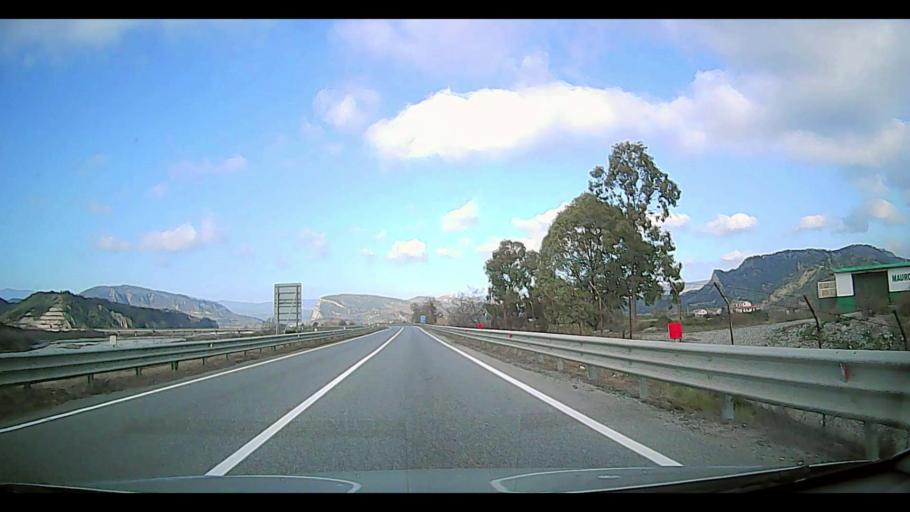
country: IT
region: Calabria
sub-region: Provincia di Crotone
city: Santa Severina
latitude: 39.1651
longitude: 16.9375
